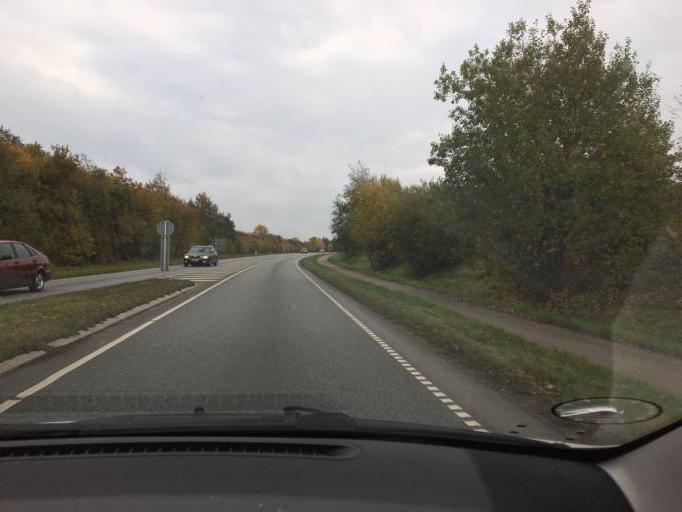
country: DK
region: South Denmark
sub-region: Fredericia Kommune
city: Fredericia
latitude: 55.6072
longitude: 9.7565
